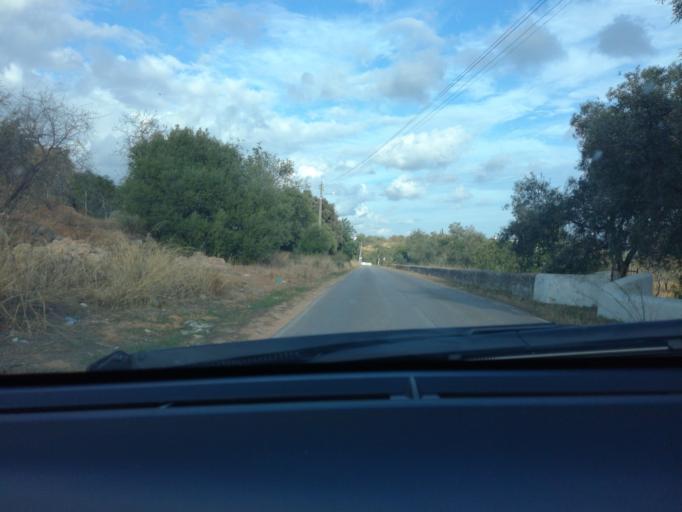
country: PT
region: Faro
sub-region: Olhao
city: Moncarapacho
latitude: 37.0821
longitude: -7.7998
